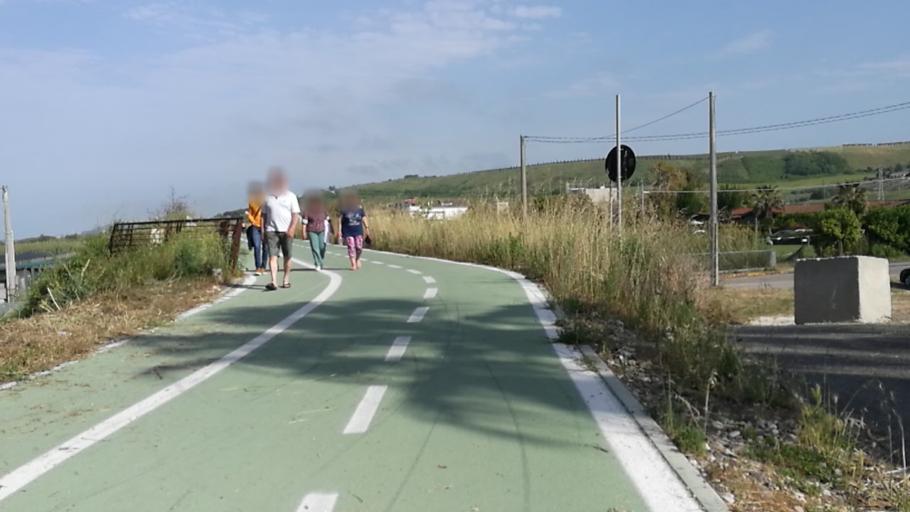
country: IT
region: Abruzzo
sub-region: Provincia di Chieti
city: Casalbordino-Miracoli
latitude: 42.2049
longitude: 14.6031
